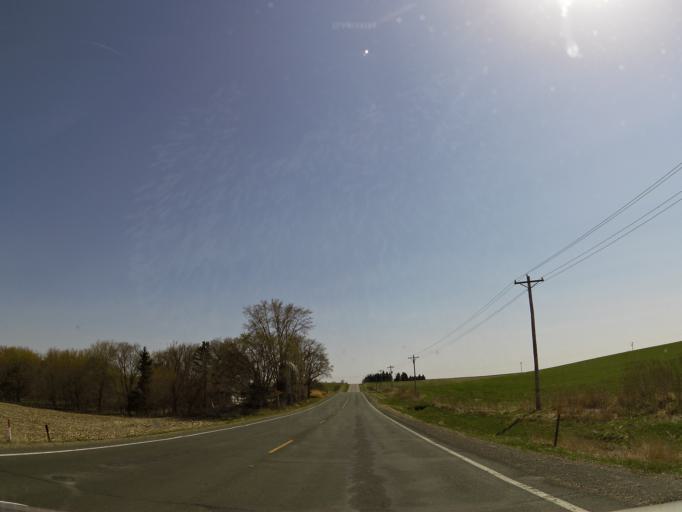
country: US
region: Wisconsin
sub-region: Saint Croix County
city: Hammond
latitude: 44.9227
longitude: -92.4355
